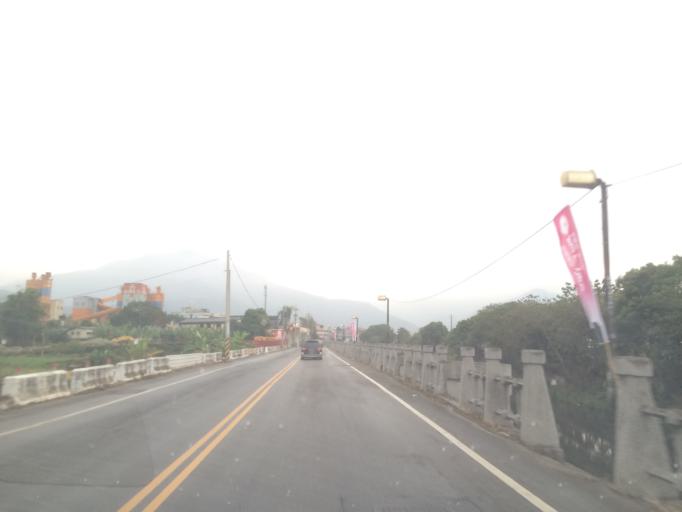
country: TW
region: Taiwan
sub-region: Nantou
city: Puli
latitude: 23.9656
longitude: 120.9556
